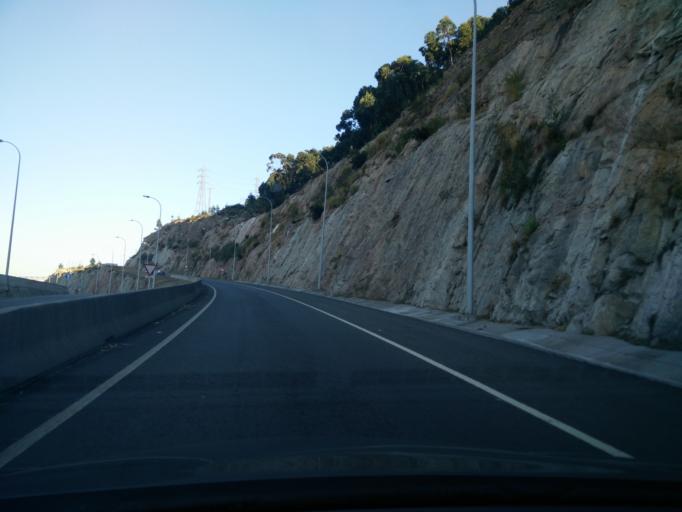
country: ES
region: Galicia
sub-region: Provincia da Coruna
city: A Coruna
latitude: 43.3422
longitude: -8.4316
